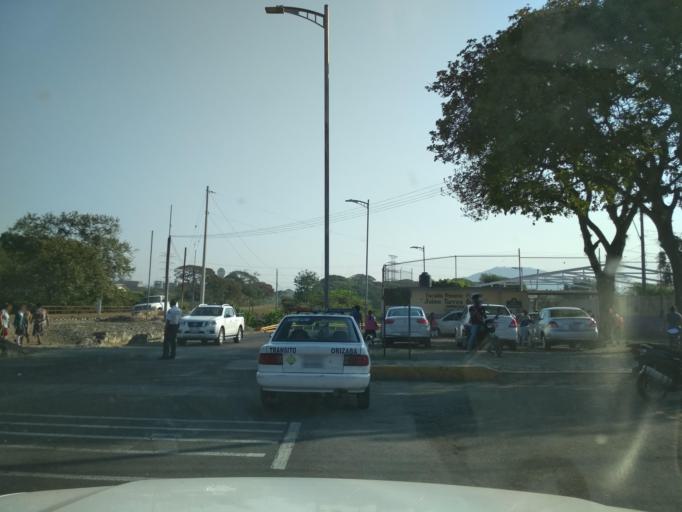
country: MX
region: Veracruz
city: Ixtac Zoquitlan
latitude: 18.8603
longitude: -97.0729
